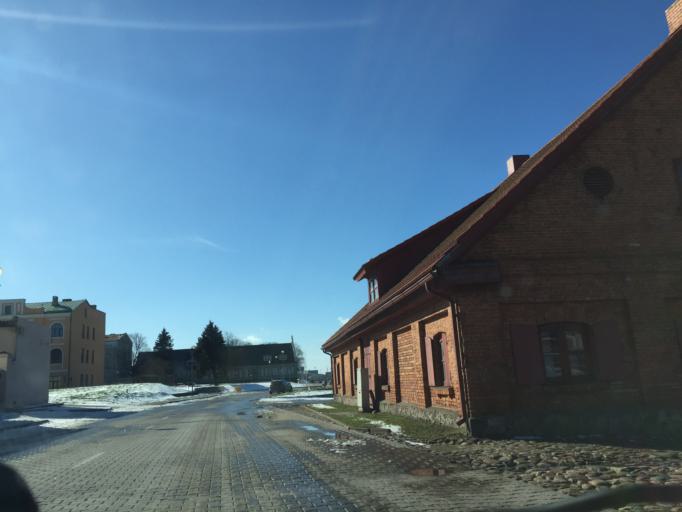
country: LV
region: Ventspils
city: Ventspils
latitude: 57.3977
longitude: 21.5643
